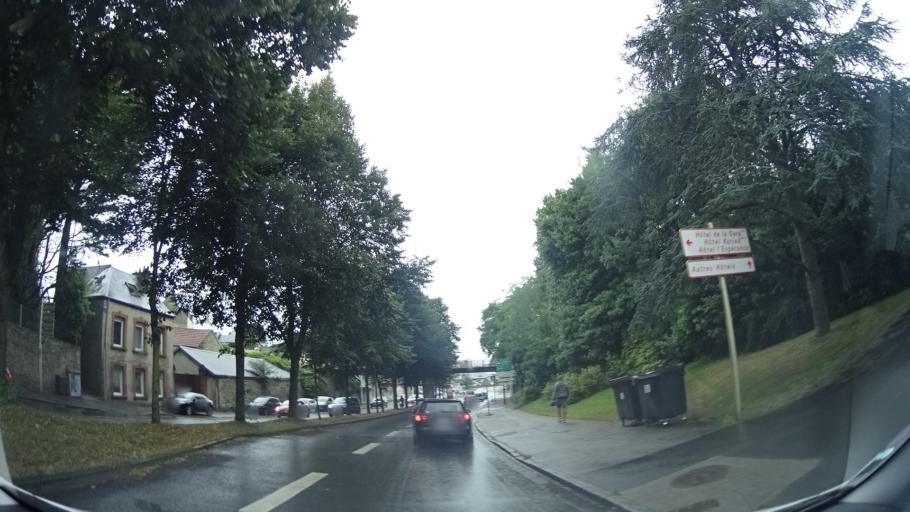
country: FR
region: Lower Normandy
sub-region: Departement de la Manche
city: Cherbourg-Octeville
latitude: 49.6323
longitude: -1.6234
